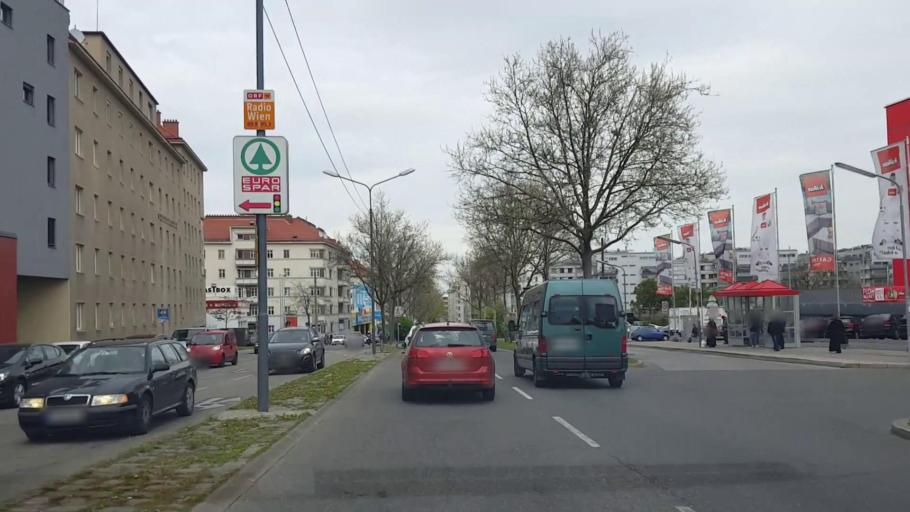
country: AT
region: Vienna
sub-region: Wien Stadt
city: Vienna
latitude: 48.1652
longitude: 16.3685
